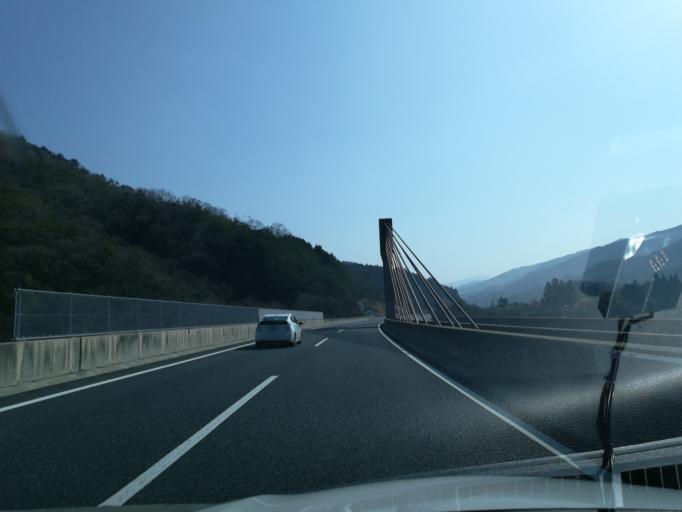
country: JP
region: Tokushima
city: Ikedacho
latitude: 34.0058
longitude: 133.7012
